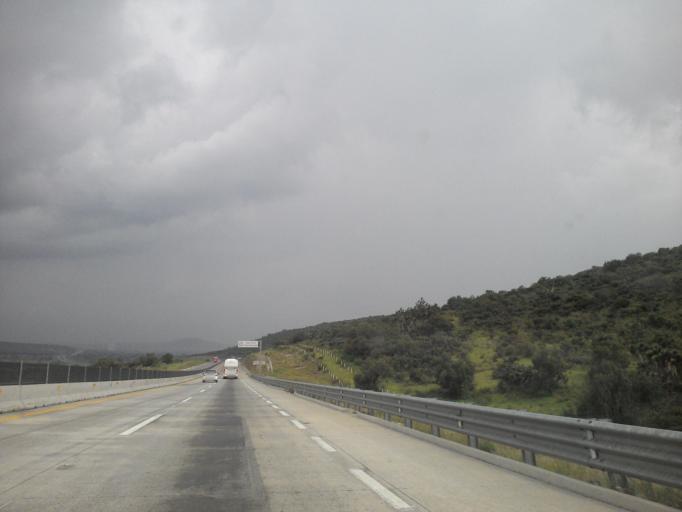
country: MX
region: Morelos
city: San Francisco Zacacalco
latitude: 19.9590
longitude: -98.9977
